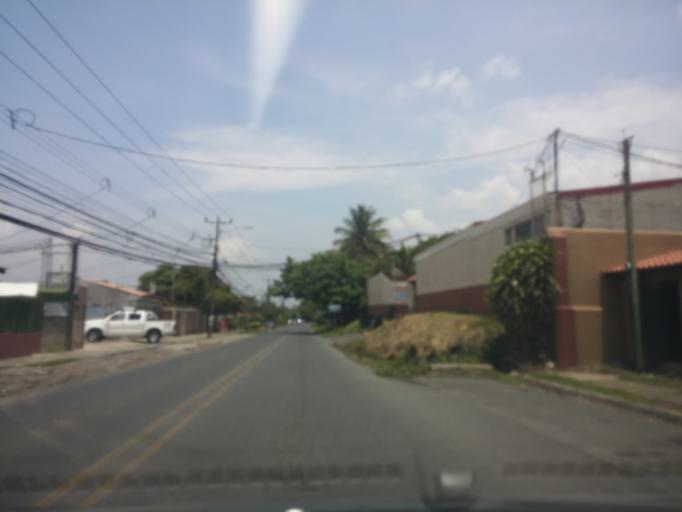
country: CR
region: Heredia
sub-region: Canton de Belen
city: San Antonio
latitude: 9.9779
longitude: -84.2019
